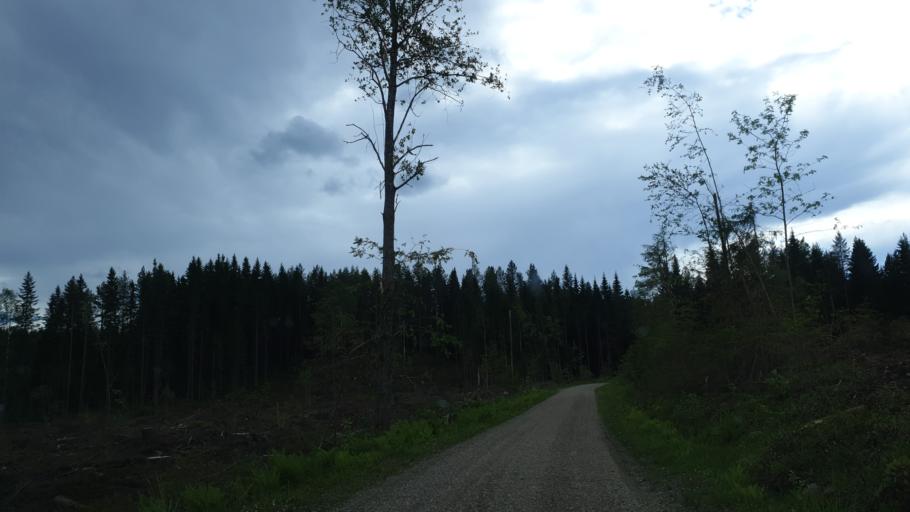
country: FI
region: Northern Savo
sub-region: Koillis-Savo
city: Kaavi
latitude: 62.9799
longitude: 28.7566
